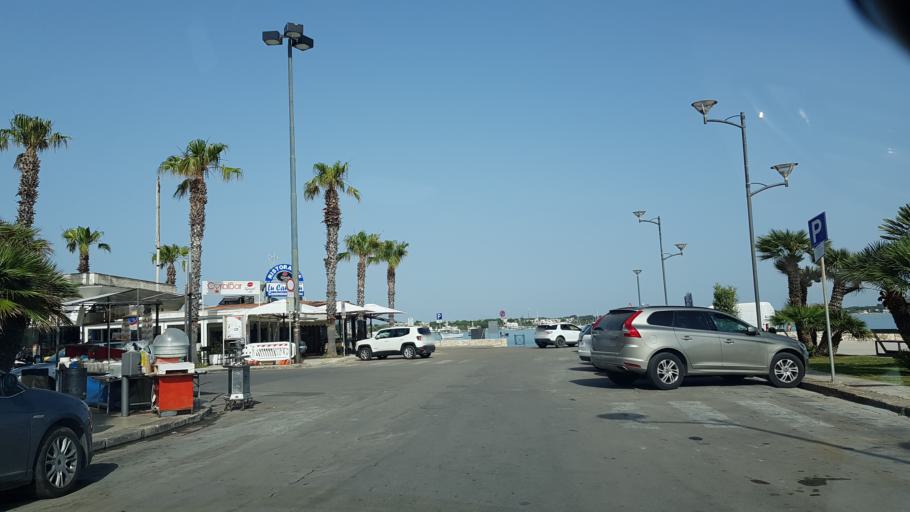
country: IT
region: Apulia
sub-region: Provincia di Lecce
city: Porto Cesareo
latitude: 40.2571
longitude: 17.8923
